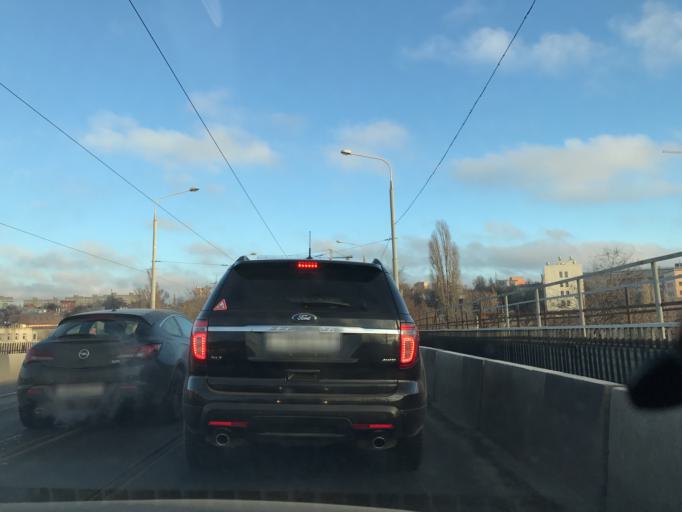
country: RU
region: Rostov
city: Rostov-na-Donu
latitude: 47.2228
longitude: 39.6855
